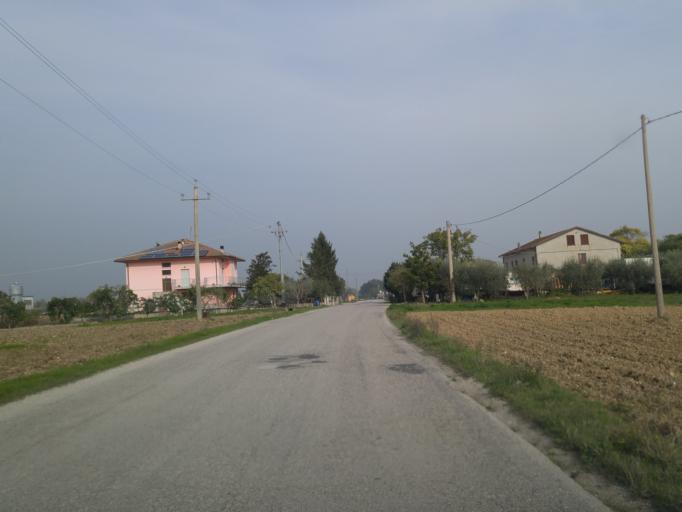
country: IT
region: The Marches
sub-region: Provincia di Pesaro e Urbino
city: Lucrezia
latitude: 43.7661
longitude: 12.9625
